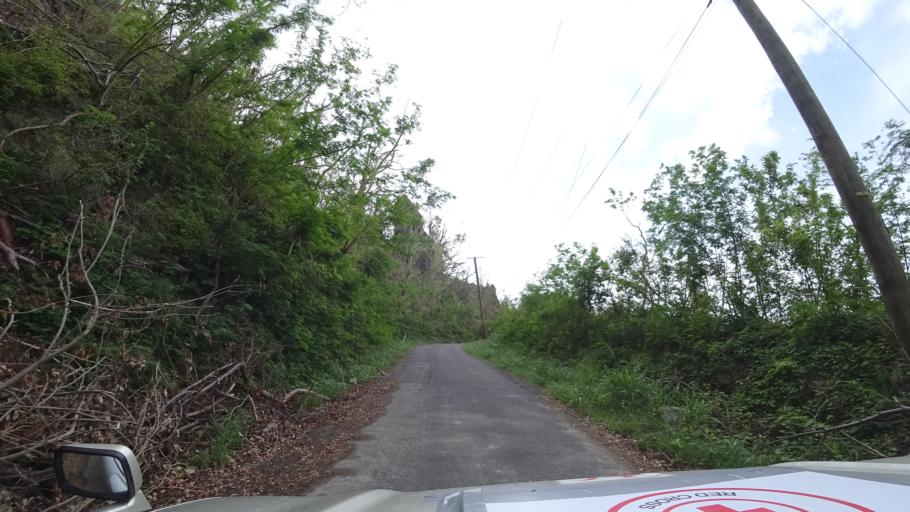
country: DM
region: Saint Luke
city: Pointe Michel
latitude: 15.2440
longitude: -61.3723
